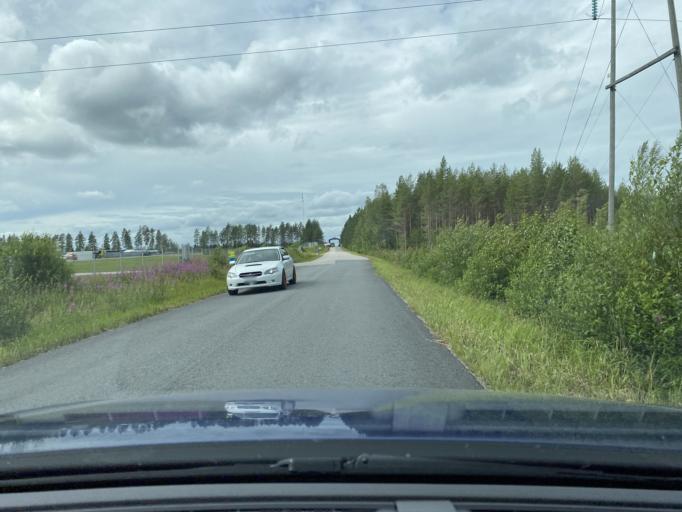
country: FI
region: Southern Ostrobothnia
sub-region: Seinaejoki
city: Jurva
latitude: 62.6268
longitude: 22.0205
